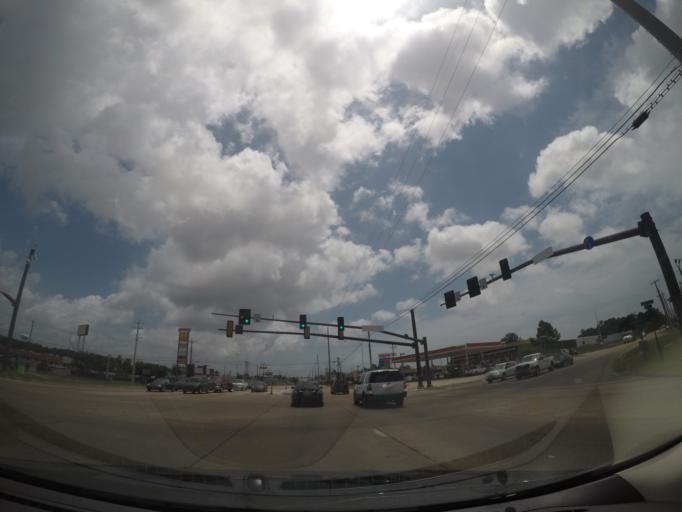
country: US
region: Mississippi
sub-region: Hancock County
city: Waveland
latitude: 30.3059
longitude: -89.3785
